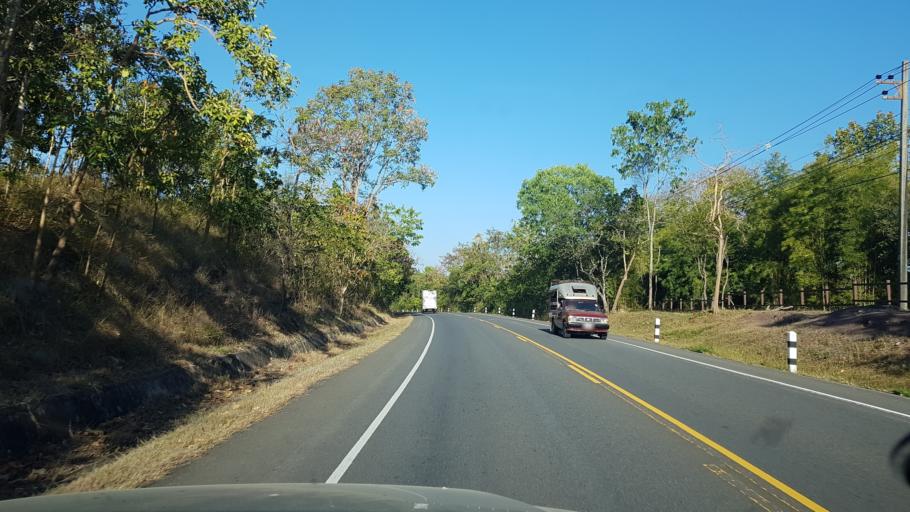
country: TH
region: Phetchabun
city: Nam Nao
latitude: 16.7540
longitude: 101.4610
